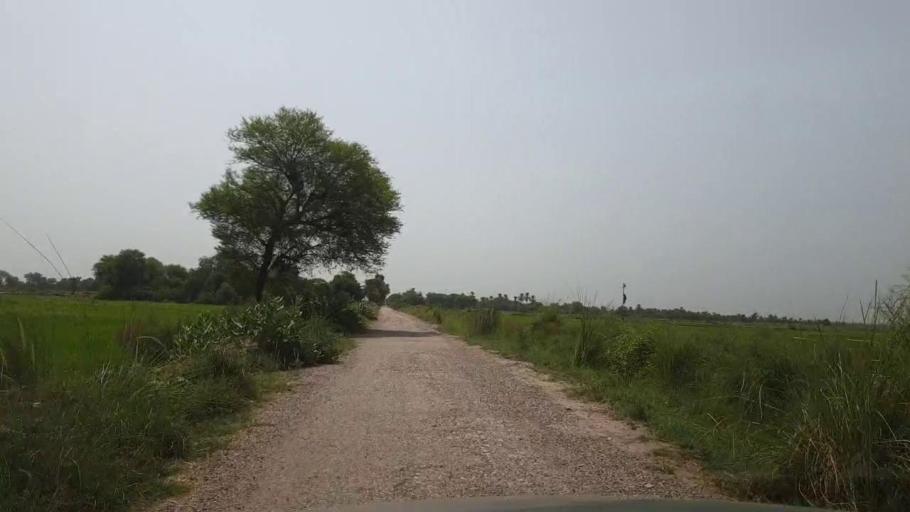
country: PK
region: Sindh
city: Madeji
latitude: 27.8294
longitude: 68.4304
